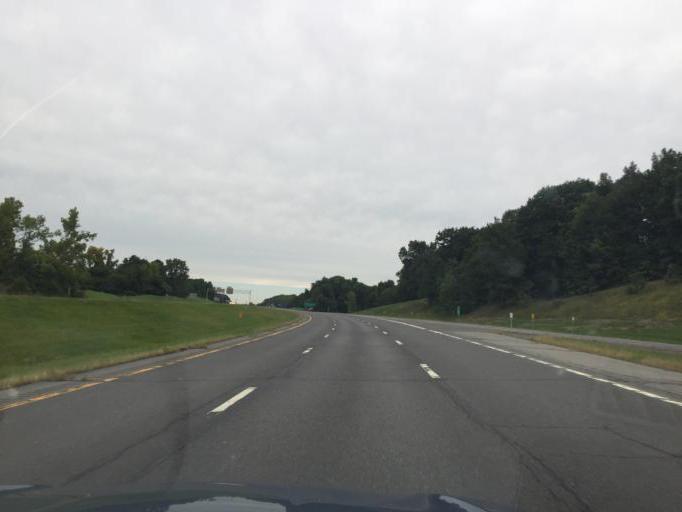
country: US
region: New York
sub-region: Rensselaer County
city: East Greenbush
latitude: 42.5603
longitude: -73.6788
